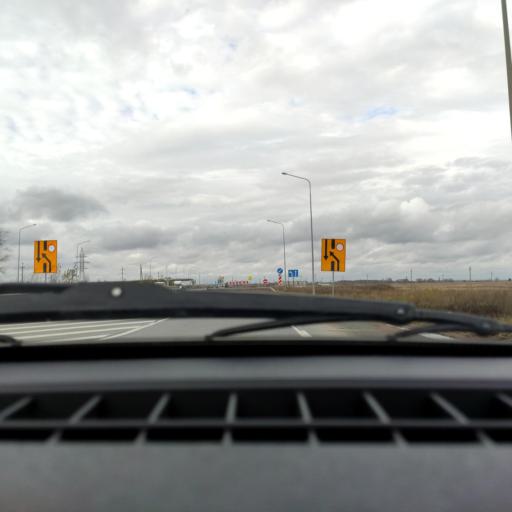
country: RU
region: Bashkortostan
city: Asanovo
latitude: 54.8990
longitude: 55.6340
